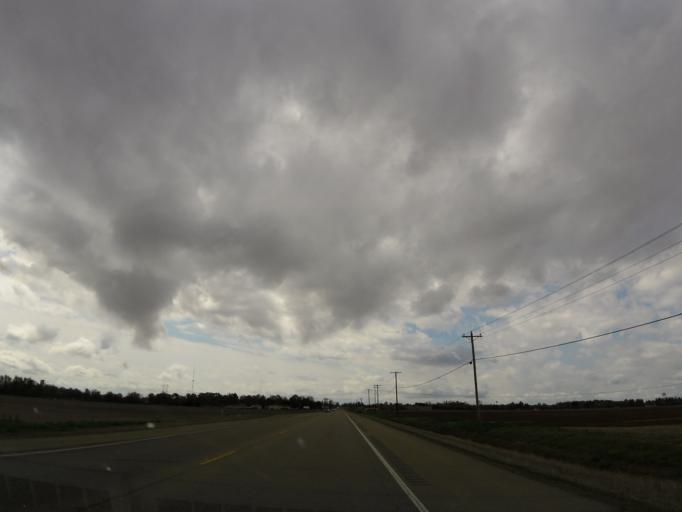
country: US
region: Arkansas
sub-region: Clay County
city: Corning
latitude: 36.4324
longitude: -90.5859
